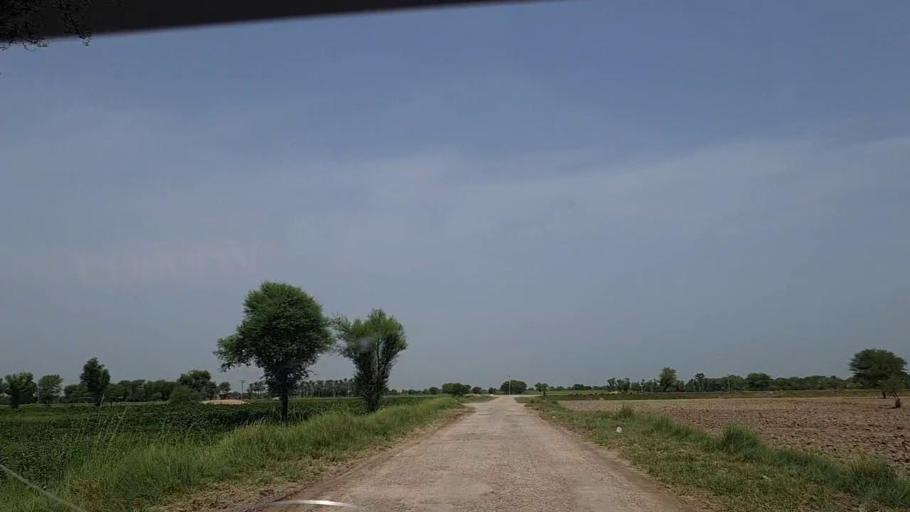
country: PK
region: Sindh
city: Tharu Shah
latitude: 26.9199
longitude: 68.0538
